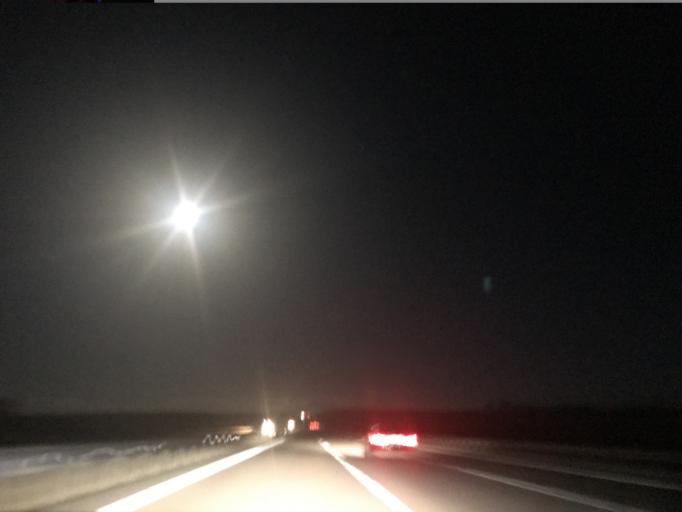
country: TR
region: Nigde
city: Ulukisla
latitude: 37.6394
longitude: 34.3888
